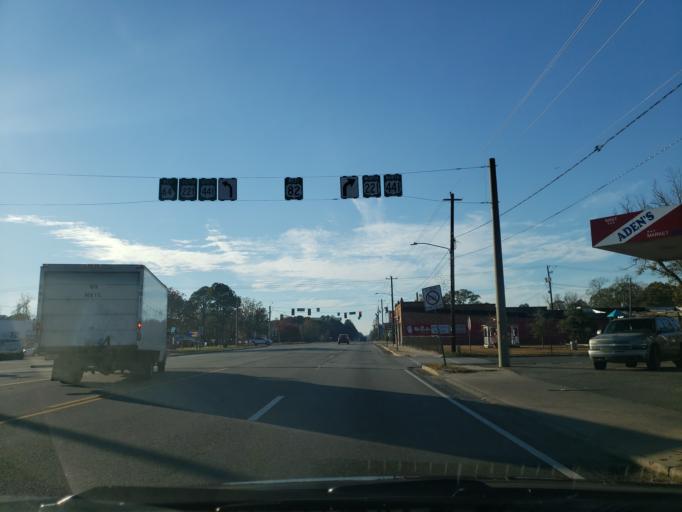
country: US
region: Georgia
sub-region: Atkinson County
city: Pearson
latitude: 31.2976
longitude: -82.8514
